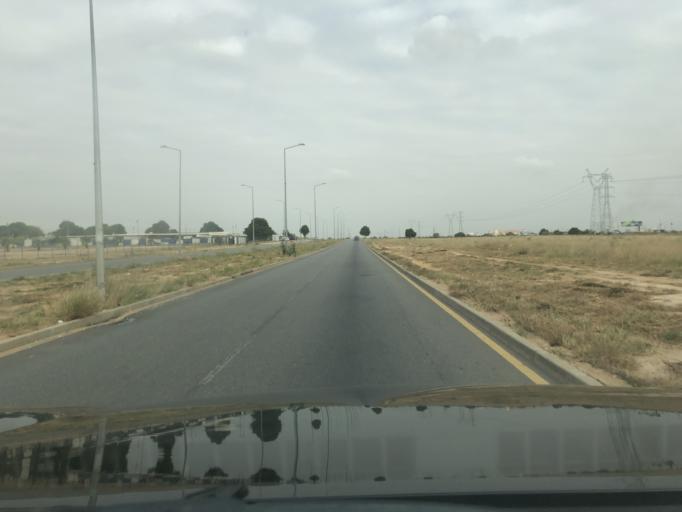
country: AO
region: Luanda
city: Luanda
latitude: -8.9757
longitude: 13.2840
